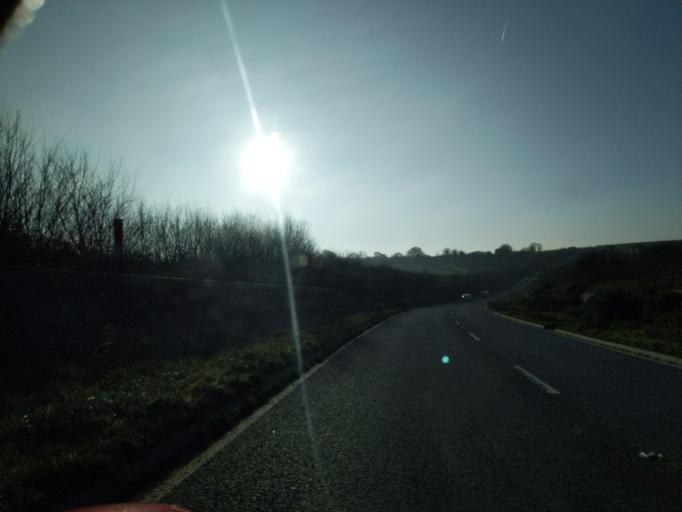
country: GB
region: England
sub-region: Cornwall
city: Liskeard
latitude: 50.4560
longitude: -4.5276
